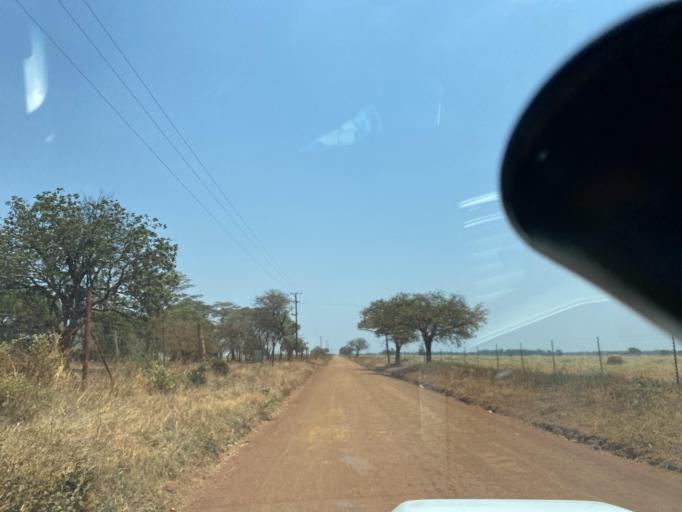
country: ZM
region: Lusaka
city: Lusaka
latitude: -15.4402
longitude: 28.0582
